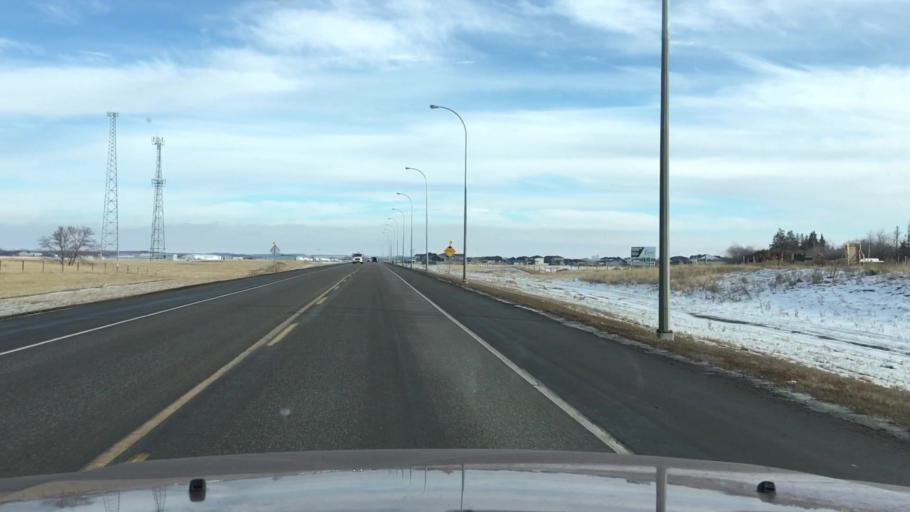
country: CA
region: Saskatchewan
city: Pilot Butte
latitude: 50.4864
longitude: -104.4289
